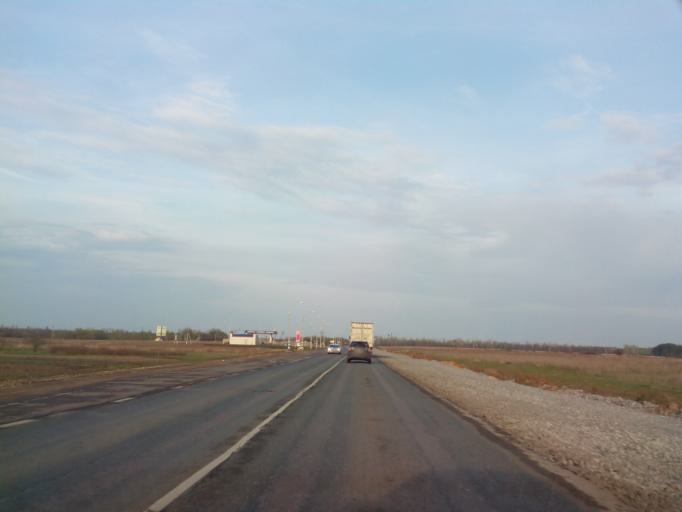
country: RU
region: Rjazan
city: Zarechnyy
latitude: 53.7522
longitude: 39.8126
